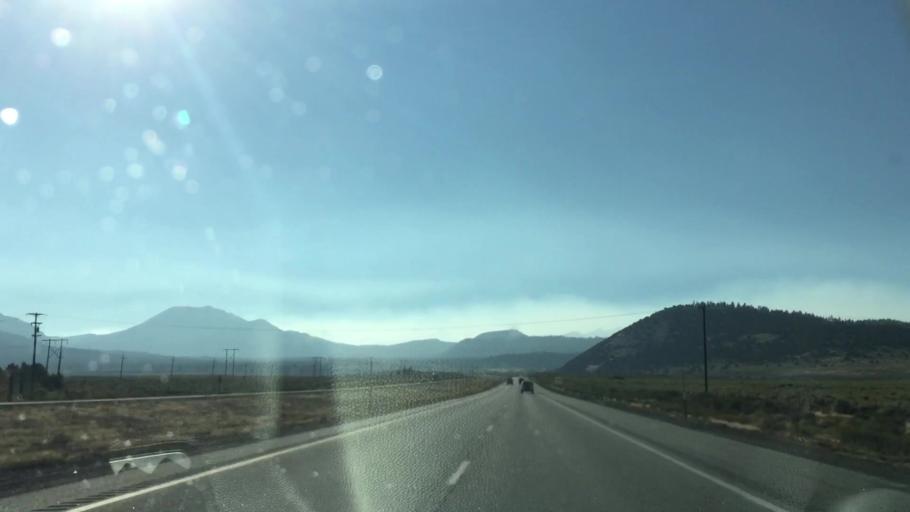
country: US
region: California
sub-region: Mono County
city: Mammoth Lakes
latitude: 37.6300
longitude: -118.8655
